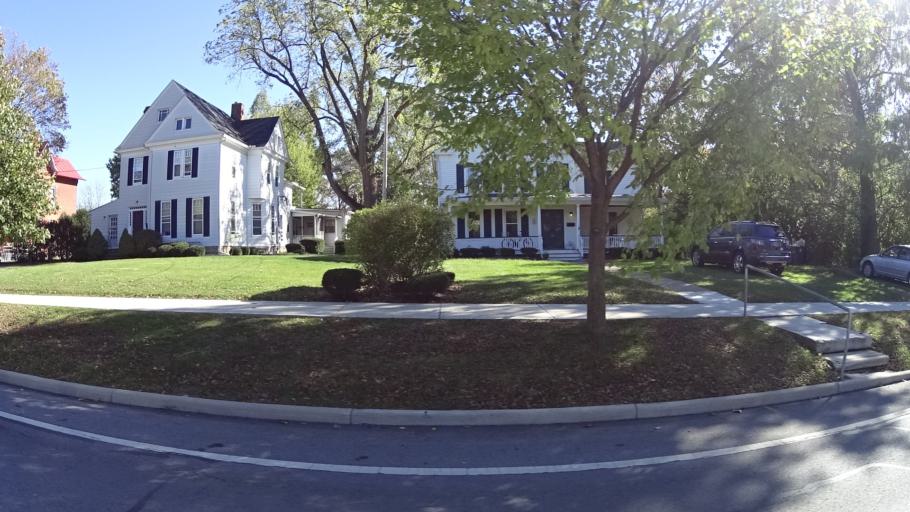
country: US
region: Ohio
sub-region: Lorain County
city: Oberlin
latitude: 41.2894
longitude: -82.2201
